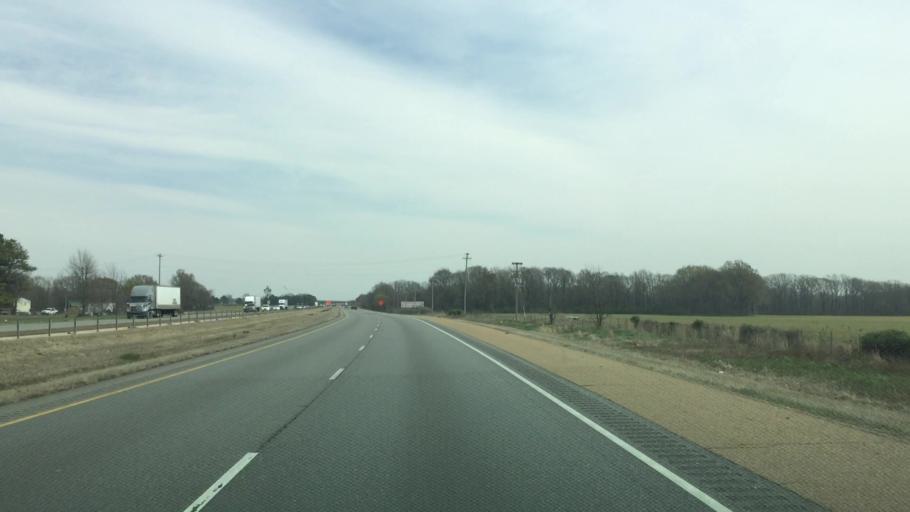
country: US
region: Arkansas
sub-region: Saint Francis County
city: Forrest City
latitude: 34.9777
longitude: -90.9190
